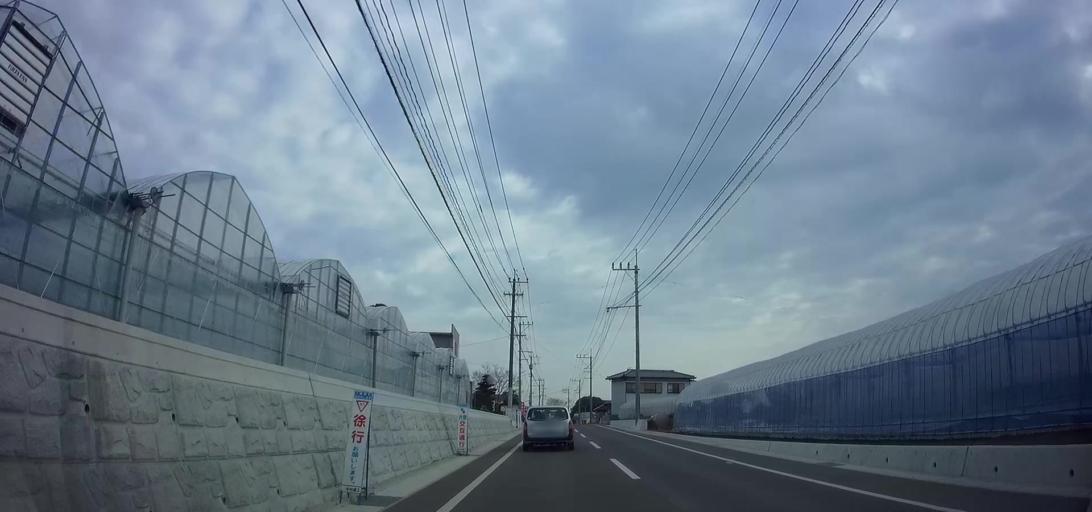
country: JP
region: Nagasaki
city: Shimabara
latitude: 32.6917
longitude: 130.3190
